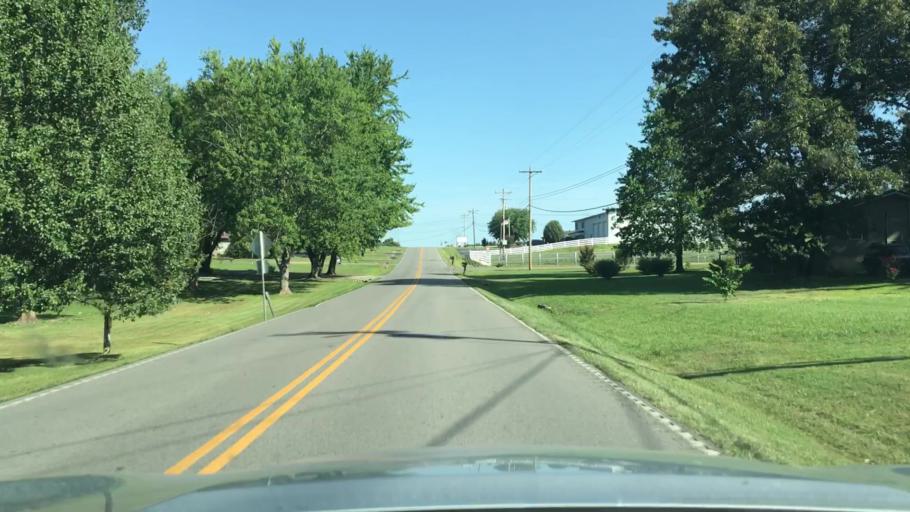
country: US
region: Kentucky
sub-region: Muhlenberg County
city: Greenville
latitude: 37.1635
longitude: -87.1439
